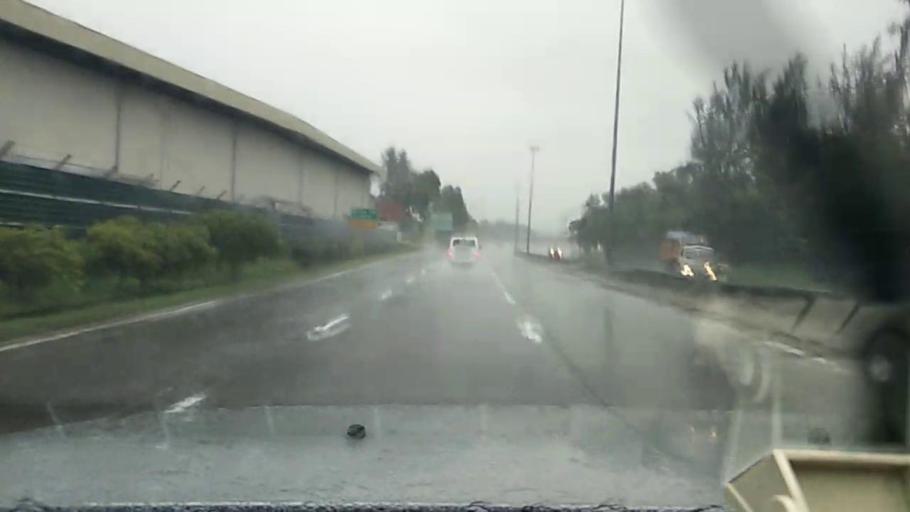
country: MY
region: Selangor
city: Kampong Baharu Balakong
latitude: 3.0032
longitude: 101.7728
